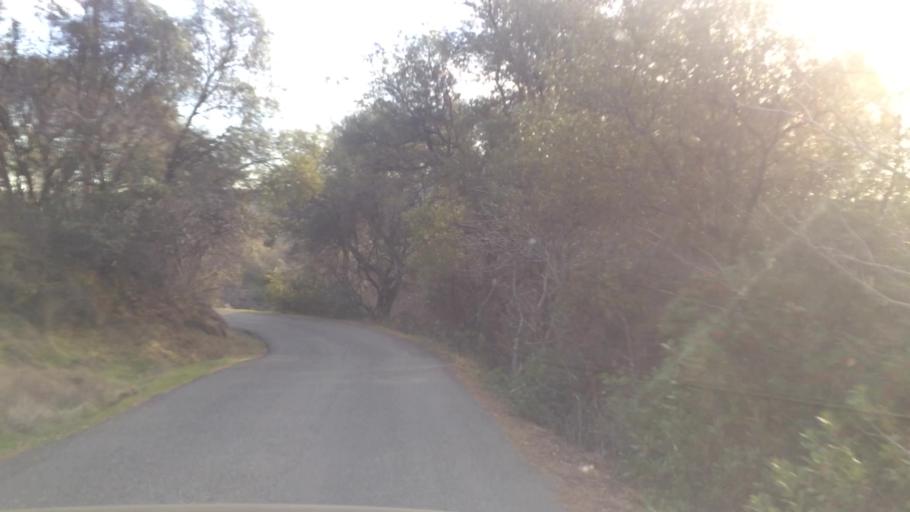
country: US
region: California
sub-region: Nevada County
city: Penn Valley
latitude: 39.2130
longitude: -121.1764
